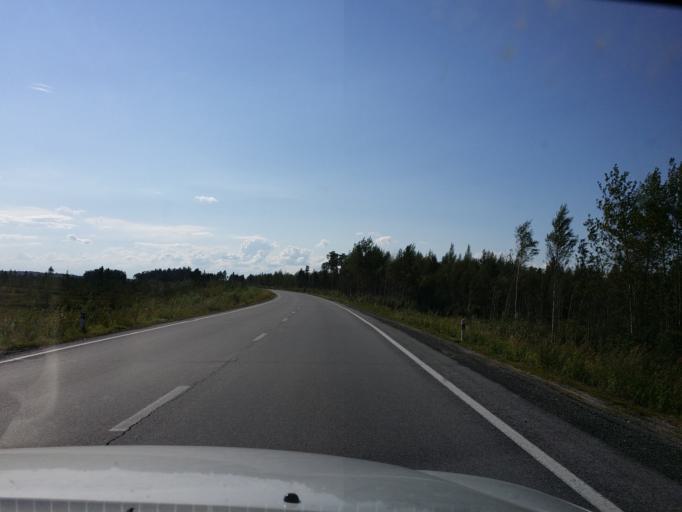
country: RU
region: Khanty-Mansiyskiy Avtonomnyy Okrug
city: Lokosovo
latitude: 61.3932
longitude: 74.9068
